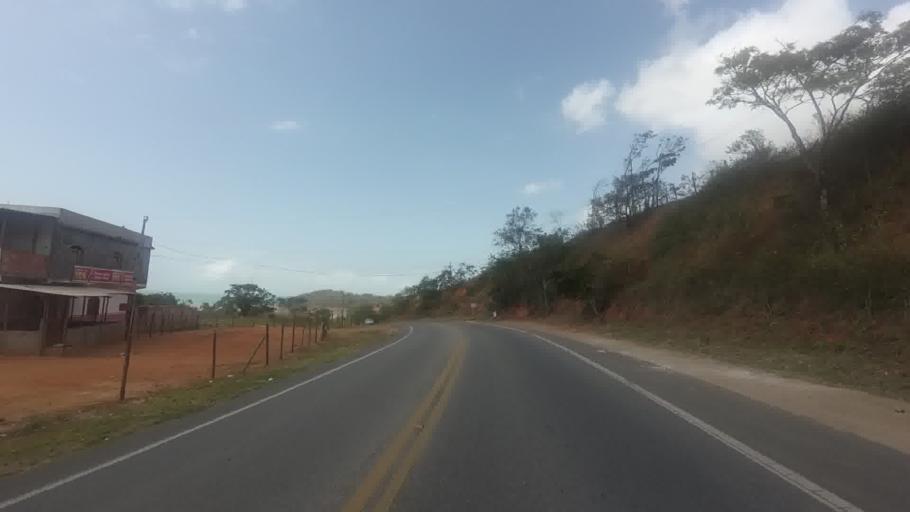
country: BR
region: Espirito Santo
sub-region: Piuma
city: Piuma
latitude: -20.8705
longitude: -40.7634
